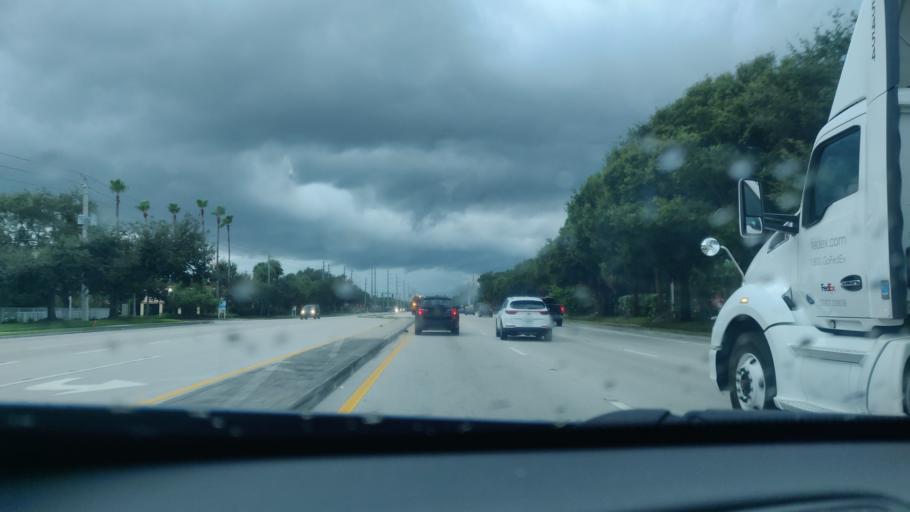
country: US
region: Florida
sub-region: Palm Beach County
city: Mangonia Park
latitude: 26.7594
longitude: -80.0975
